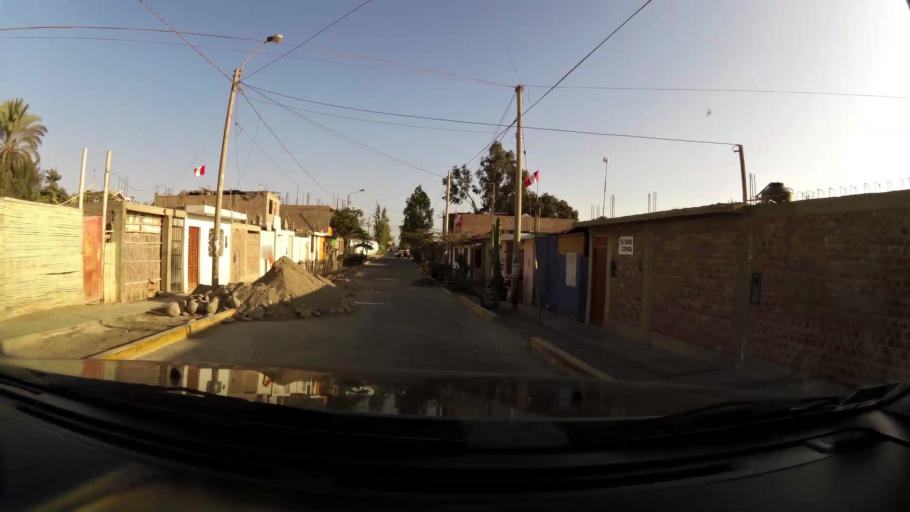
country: PE
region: Ica
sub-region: Provincia de Pisco
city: Villa Tupac Amaru
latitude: -13.7082
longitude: -76.1476
